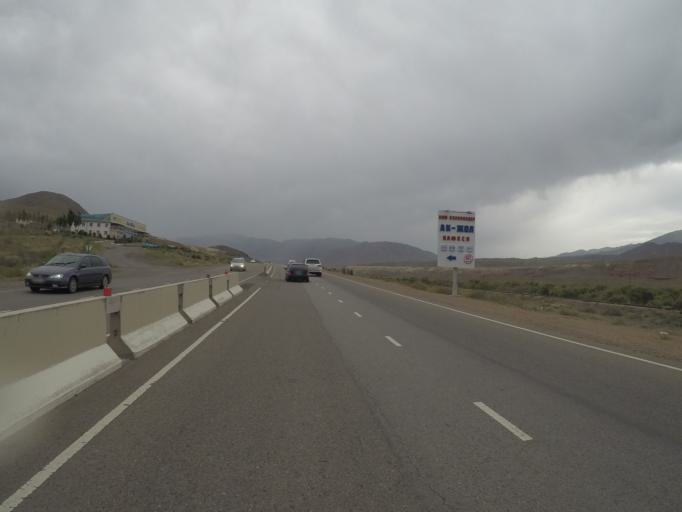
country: KG
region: Naryn
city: Kochkor
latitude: 42.5101
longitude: 75.8318
